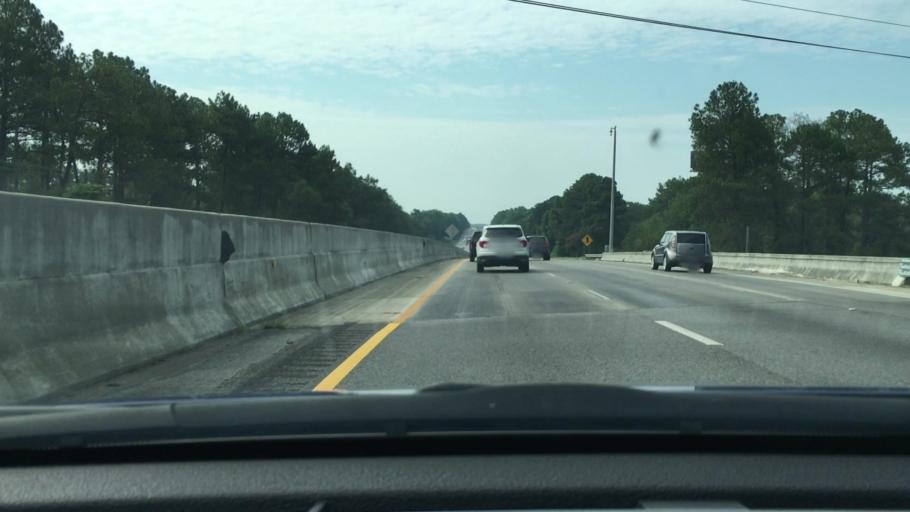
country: US
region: South Carolina
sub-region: Lexington County
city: Springdale
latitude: 33.9566
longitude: -81.0935
